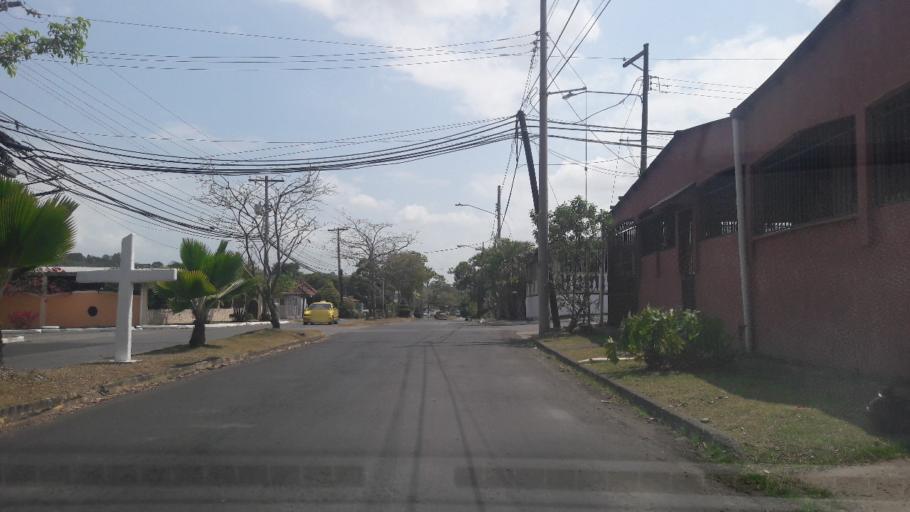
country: PA
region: Panama
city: Alcalde Diaz
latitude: 9.1319
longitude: -79.5484
